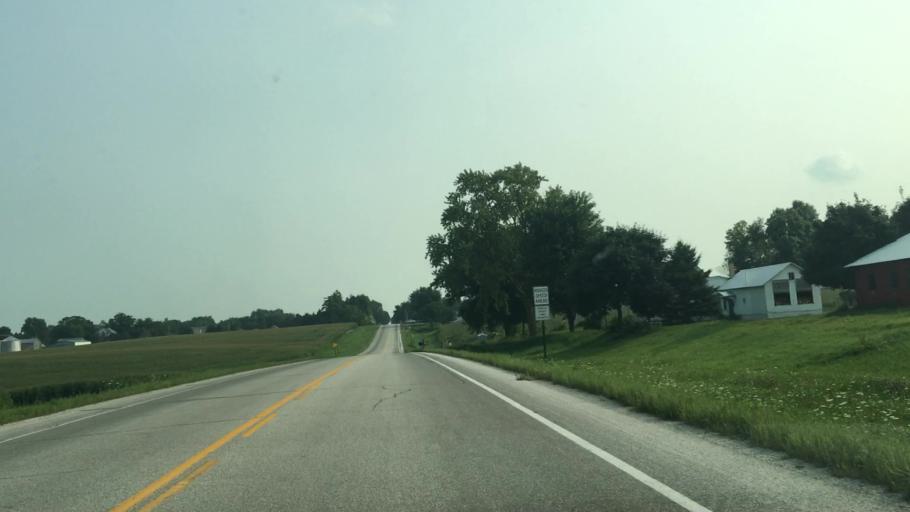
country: US
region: Minnesota
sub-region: Fillmore County
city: Harmony
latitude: 43.5384
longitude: -91.9297
